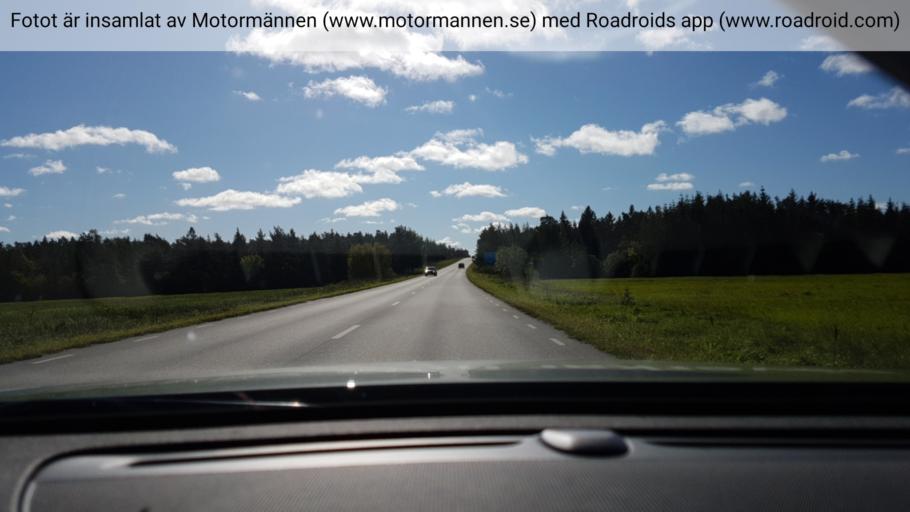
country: SE
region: Gotland
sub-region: Gotland
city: Slite
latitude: 57.7559
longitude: 18.7905
